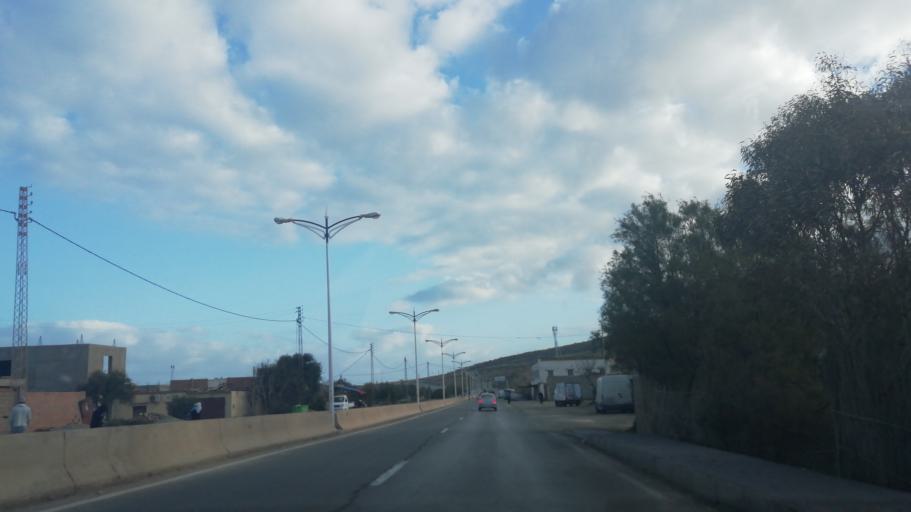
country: DZ
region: Mostaganem
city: Mostaganem
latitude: 36.0307
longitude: 0.1383
